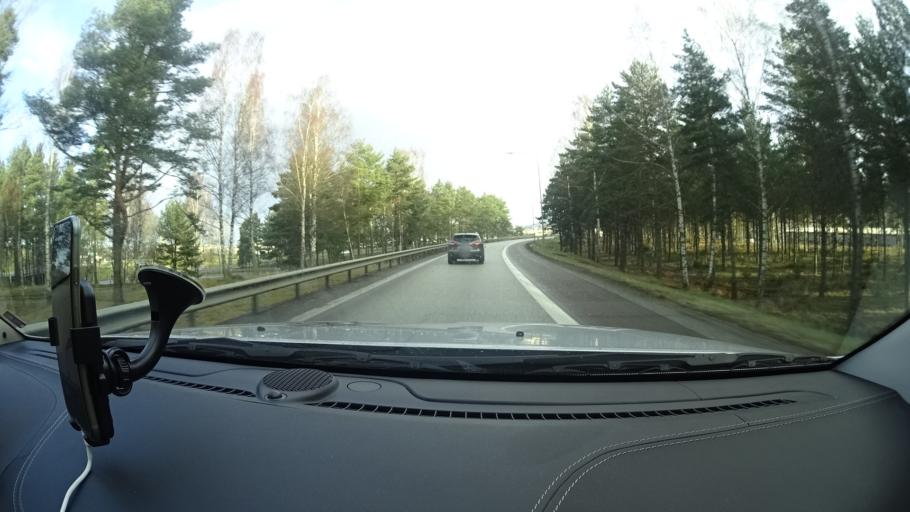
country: SE
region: Joenkoeping
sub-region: Jonkopings Kommun
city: Jonkoping
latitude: 57.7568
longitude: 14.1585
